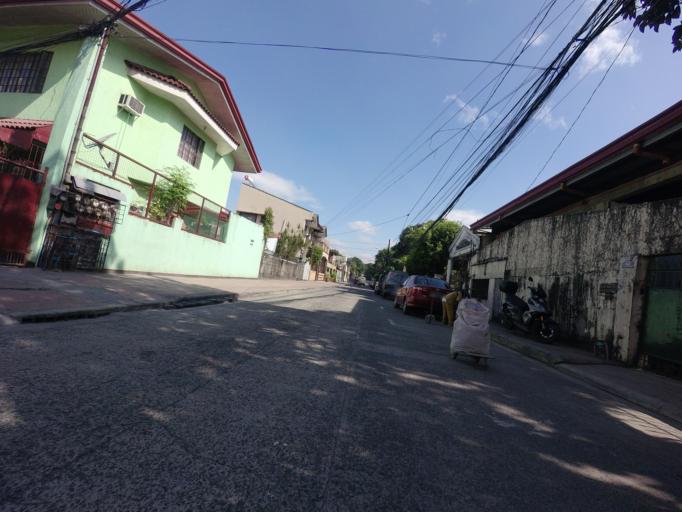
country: PH
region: Calabarzon
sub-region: Province of Rizal
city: Antipolo
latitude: 14.6422
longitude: 121.1130
